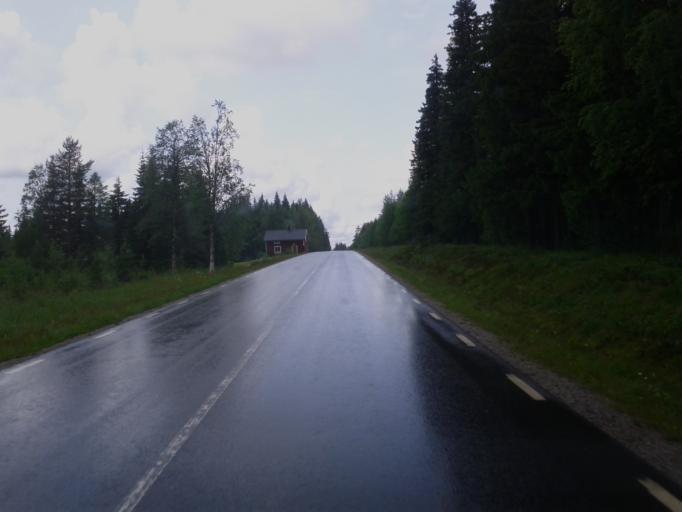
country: SE
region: Vaesterbotten
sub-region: Mala Kommun
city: Mala
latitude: 65.0947
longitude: 18.9313
